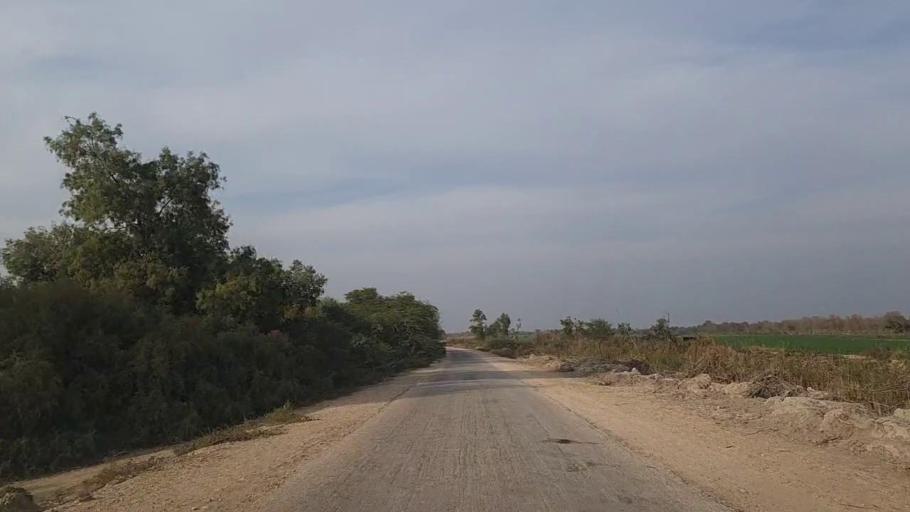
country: PK
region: Sindh
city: Daur
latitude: 26.4843
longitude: 68.4639
